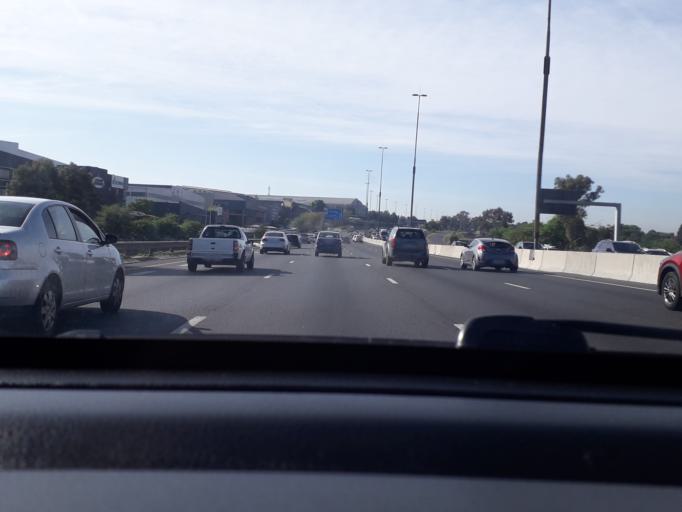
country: ZA
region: Gauteng
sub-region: City of Johannesburg Metropolitan Municipality
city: Modderfontein
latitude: -26.1081
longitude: 28.1282
